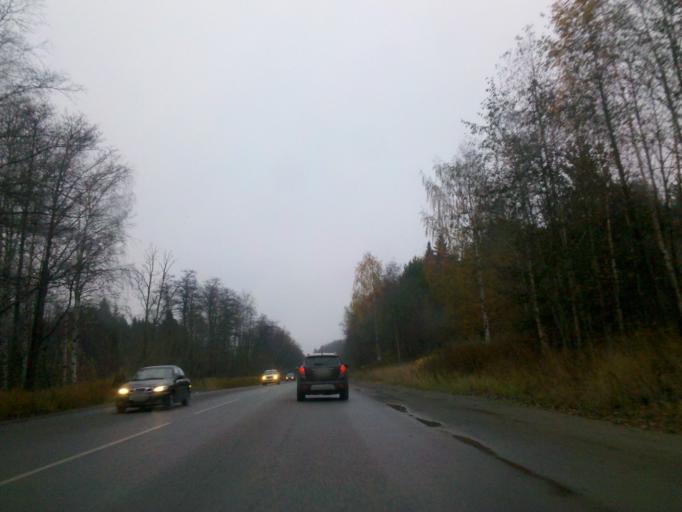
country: RU
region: Republic of Karelia
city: Petrozavodsk
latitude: 61.8209
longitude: 34.2450
